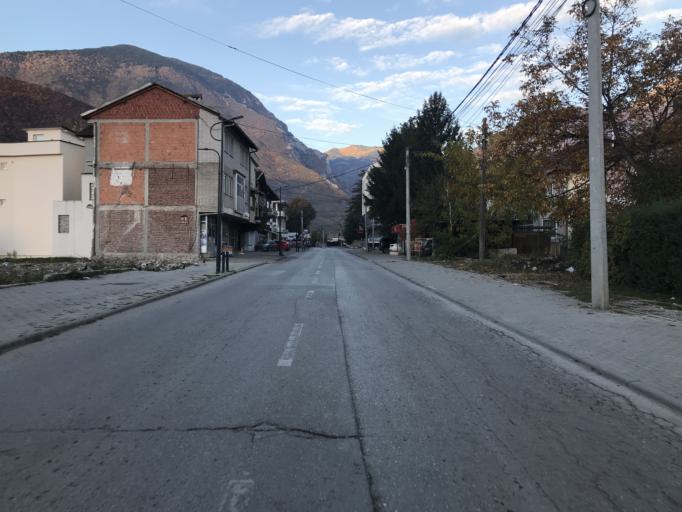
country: XK
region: Pec
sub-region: Komuna e Pejes
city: Peje
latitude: 42.6614
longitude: 20.2775
